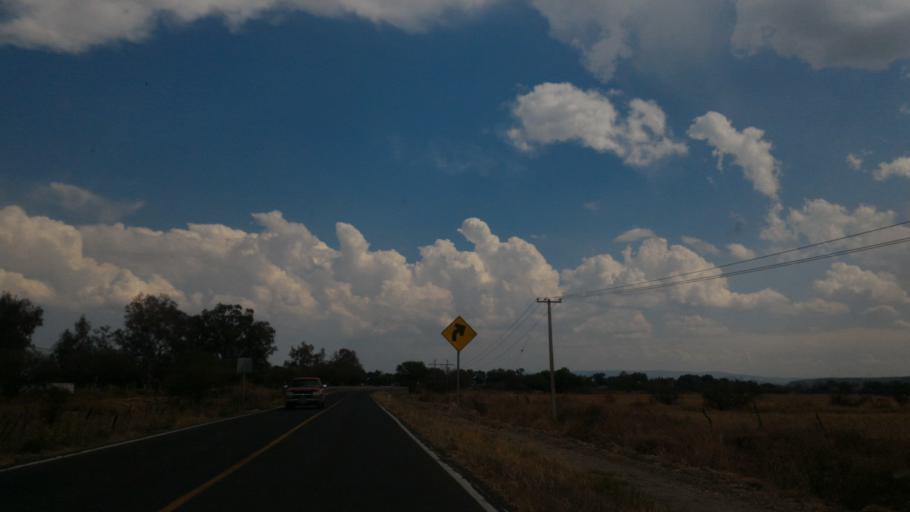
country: MX
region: Guanajuato
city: Ciudad Manuel Doblado
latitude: 20.7989
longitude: -101.9872
